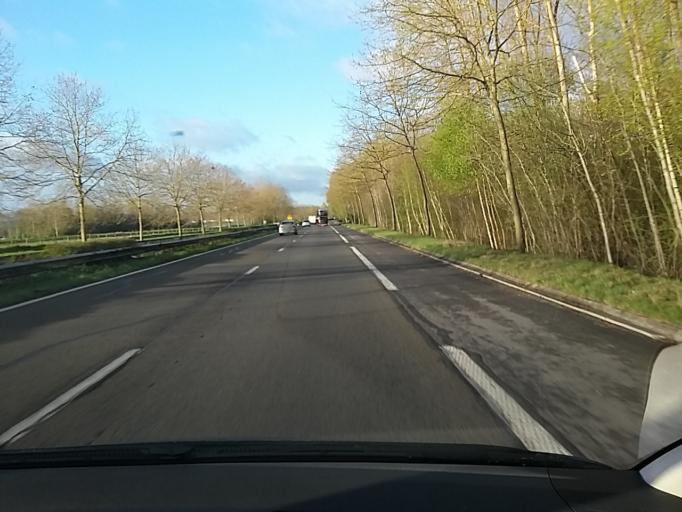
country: FR
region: Picardie
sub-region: Departement de l'Oise
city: Le Meux
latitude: 49.3442
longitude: 2.7389
